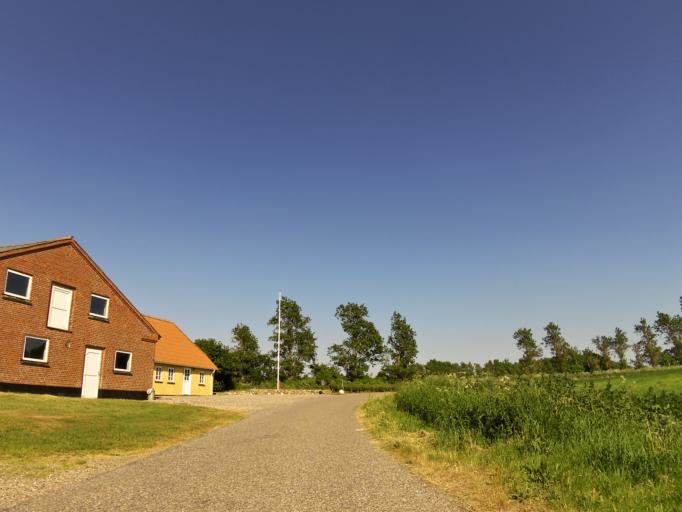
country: DK
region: Central Jutland
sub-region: Holstebro Kommune
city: Vinderup
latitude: 56.4667
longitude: 8.7053
